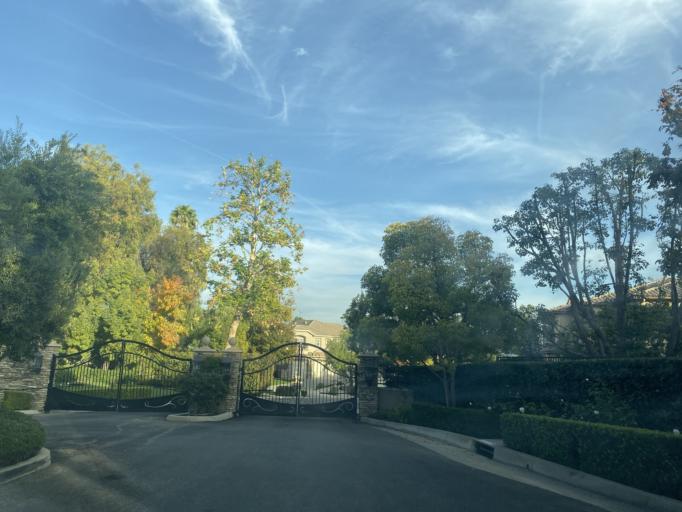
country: US
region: California
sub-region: Orange County
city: Brea
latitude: 33.8922
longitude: -117.9011
